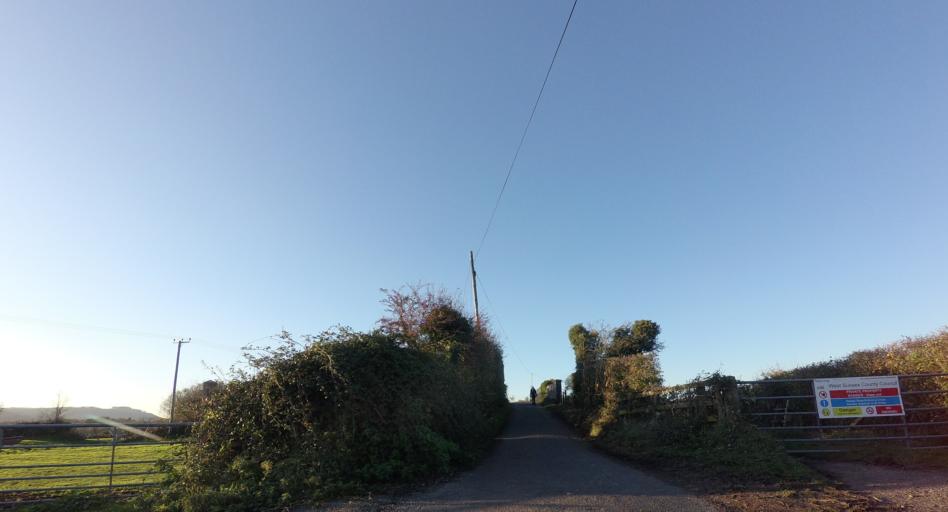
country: GB
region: England
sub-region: West Sussex
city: Steyning
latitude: 50.8969
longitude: -0.3167
